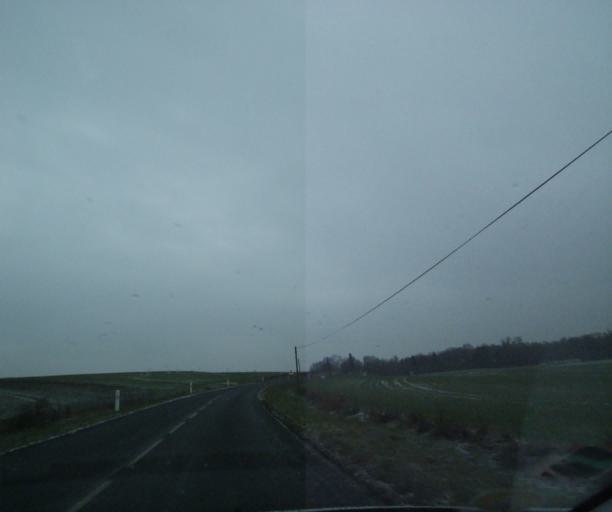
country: FR
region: Champagne-Ardenne
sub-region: Departement de la Haute-Marne
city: Wassy
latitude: 48.4513
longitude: 4.9607
